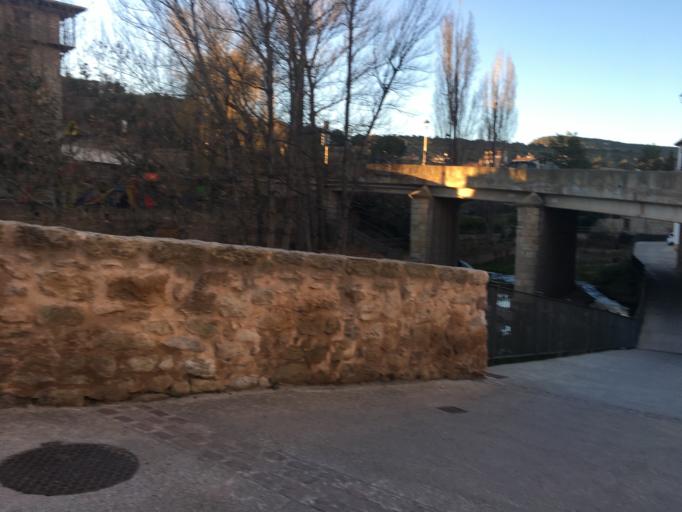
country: ES
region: Aragon
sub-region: Provincia de Teruel
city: Mora de Rubielos
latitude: 40.2507
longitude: -0.7540
